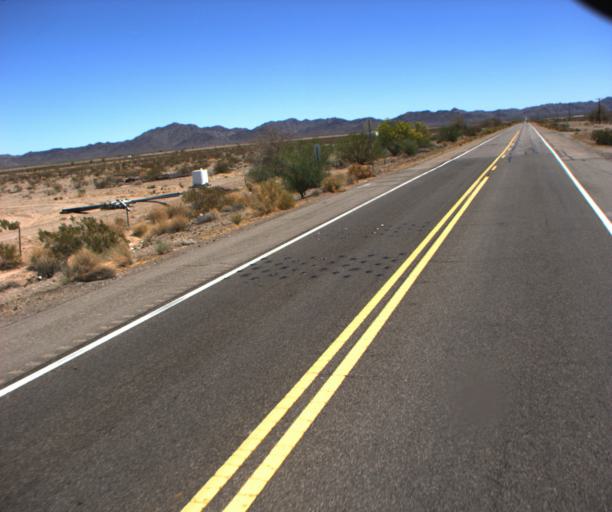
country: US
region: Arizona
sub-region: La Paz County
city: Salome
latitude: 33.7186
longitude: -113.7650
